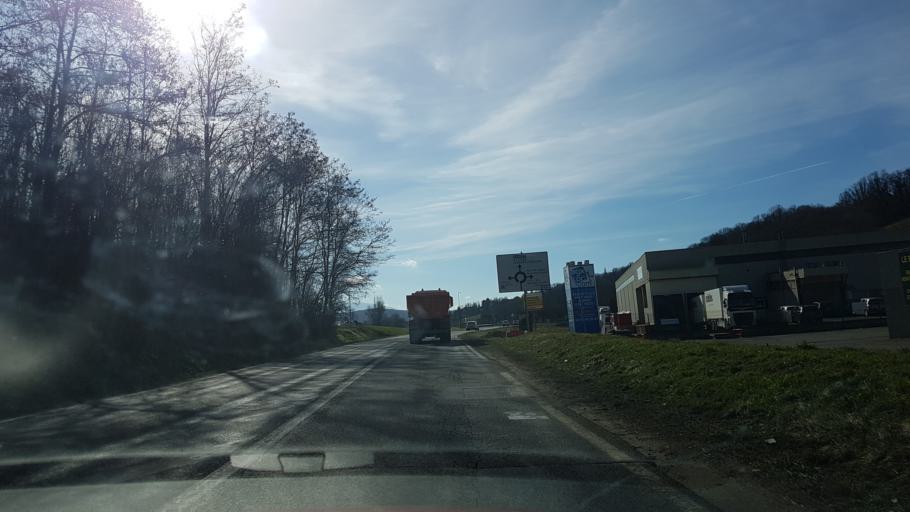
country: FR
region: Rhone-Alpes
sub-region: Departement de la Haute-Savoie
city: La Balme-de-Sillingy
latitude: 45.9739
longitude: 6.0326
